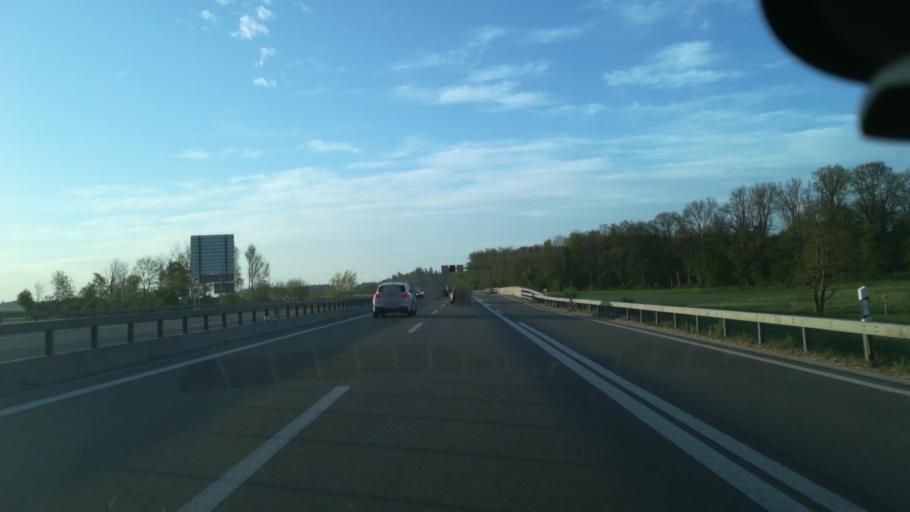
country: CH
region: Zurich
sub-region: Bezirk Andelfingen
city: Marthalen
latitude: 47.6443
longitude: 8.6522
